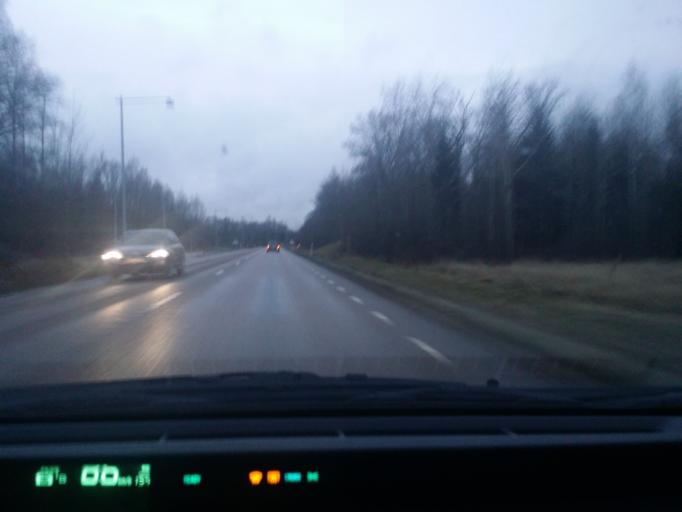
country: SE
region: Soedermanland
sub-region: Eskilstuna Kommun
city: Kvicksund
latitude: 59.4705
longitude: 16.3100
